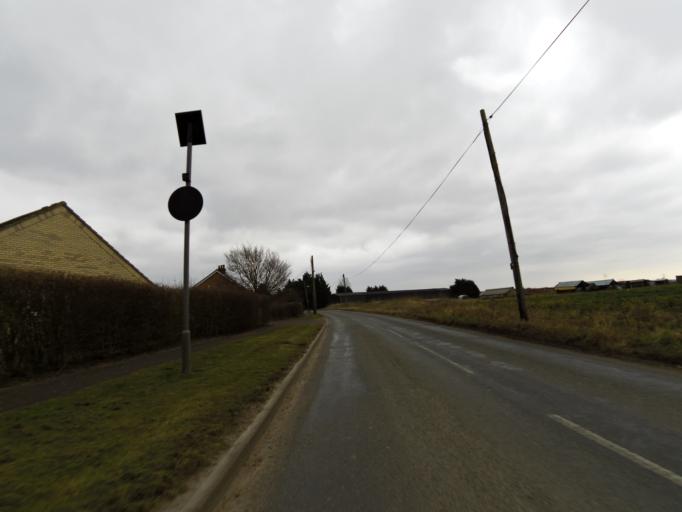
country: GB
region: England
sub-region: Suffolk
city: Ipswich
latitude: 52.1203
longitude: 1.1493
